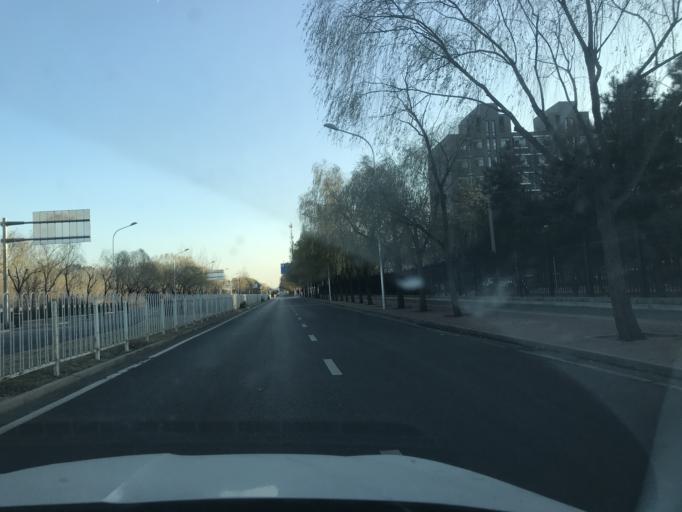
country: CN
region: Beijing
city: Xibeiwang
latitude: 40.0748
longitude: 116.2482
